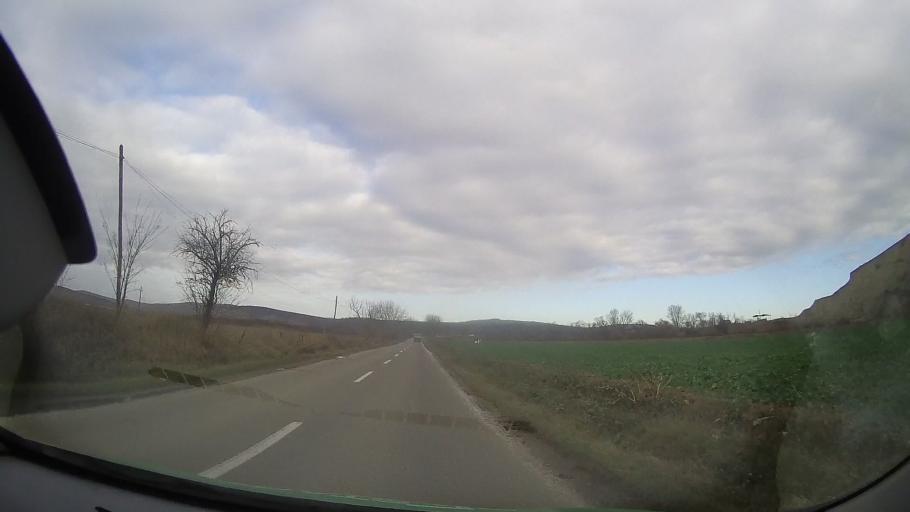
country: RO
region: Mures
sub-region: Comuna Iernut
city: Iernut
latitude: 46.4662
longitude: 24.2183
